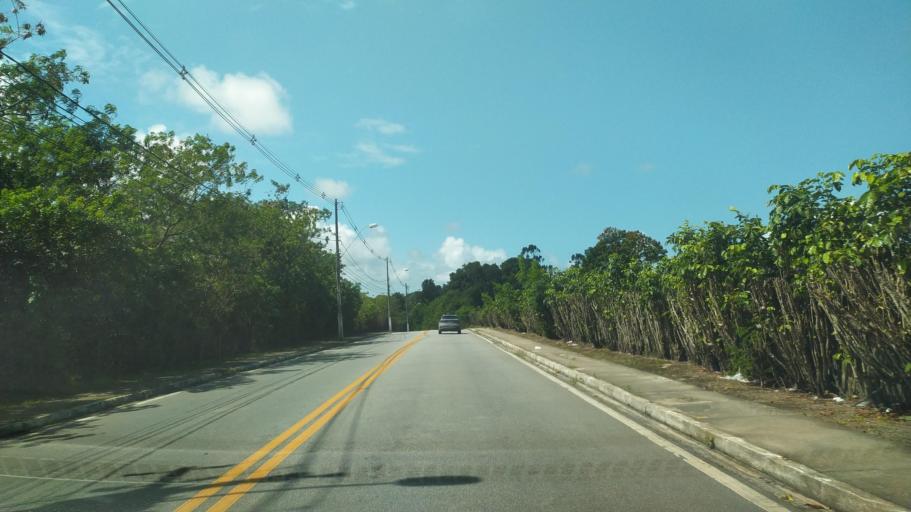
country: BR
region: Alagoas
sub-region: Maceio
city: Maceio
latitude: -9.6026
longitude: -35.7408
